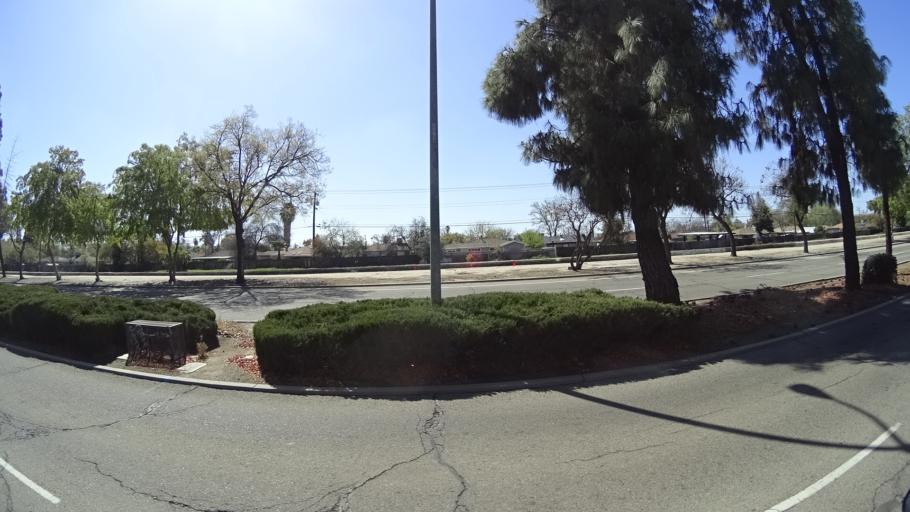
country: US
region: California
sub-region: Fresno County
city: Sunnyside
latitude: 36.7653
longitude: -119.7250
